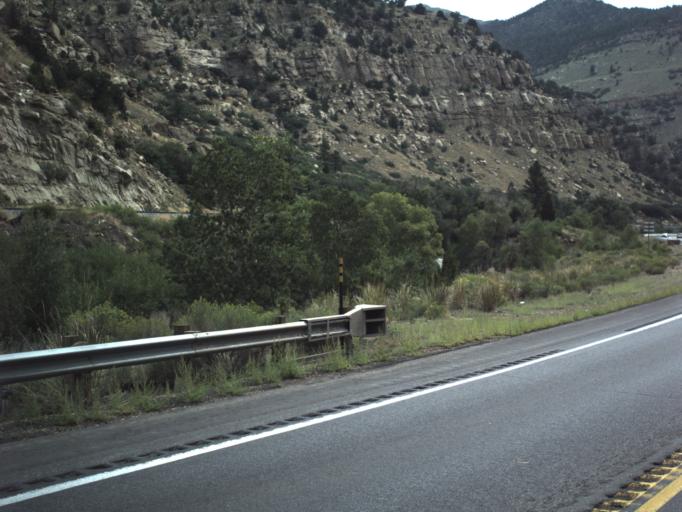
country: US
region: Utah
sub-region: Carbon County
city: Helper
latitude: 39.7640
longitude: -110.9023
